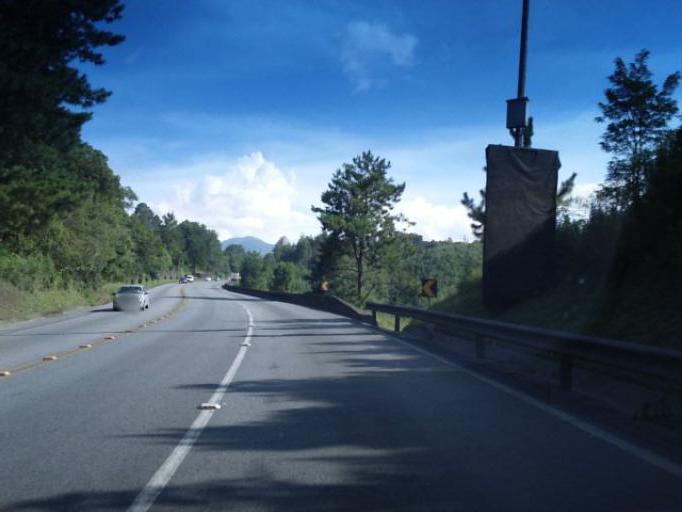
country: BR
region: Parana
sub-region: Campina Grande Do Sul
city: Campina Grande do Sul
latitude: -25.1857
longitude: -48.8861
